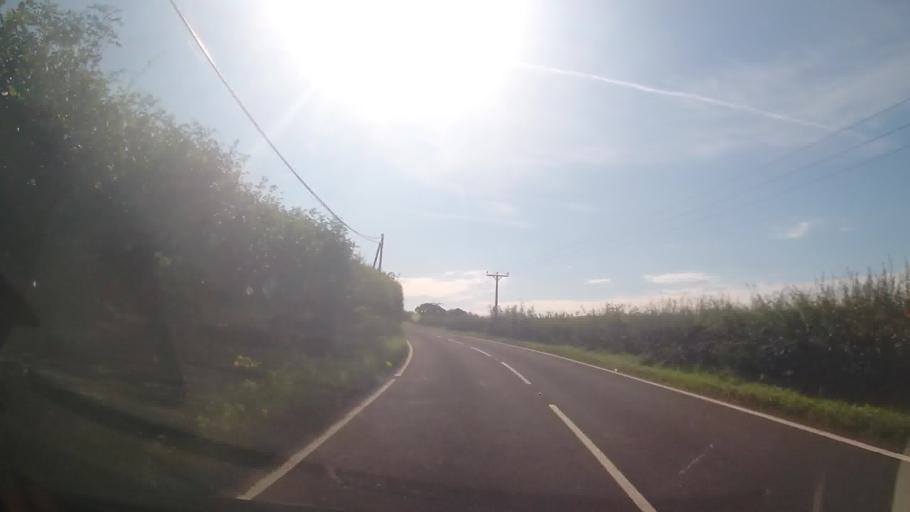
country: GB
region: Wales
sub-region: Sir Powys
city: Mochdre
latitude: 52.4933
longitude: -3.3393
